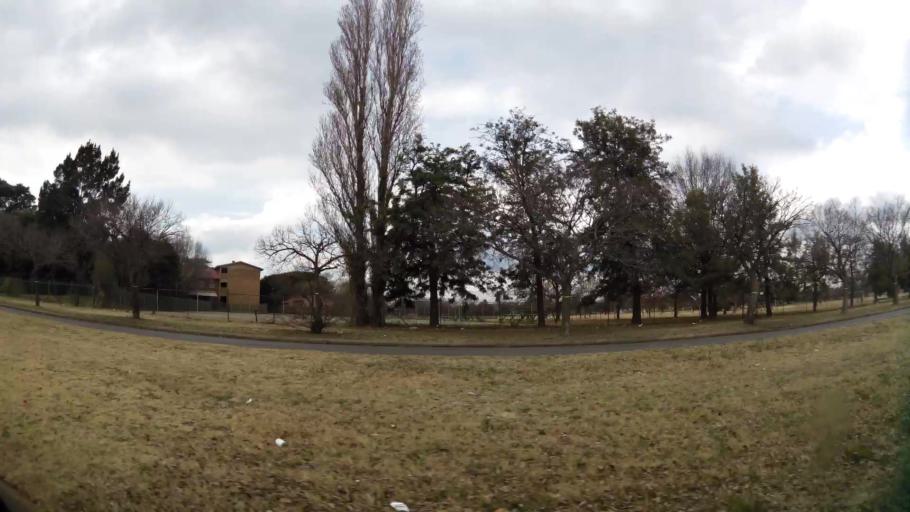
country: ZA
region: Gauteng
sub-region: Sedibeng District Municipality
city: Vanderbijlpark
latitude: -26.7141
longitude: 27.8238
